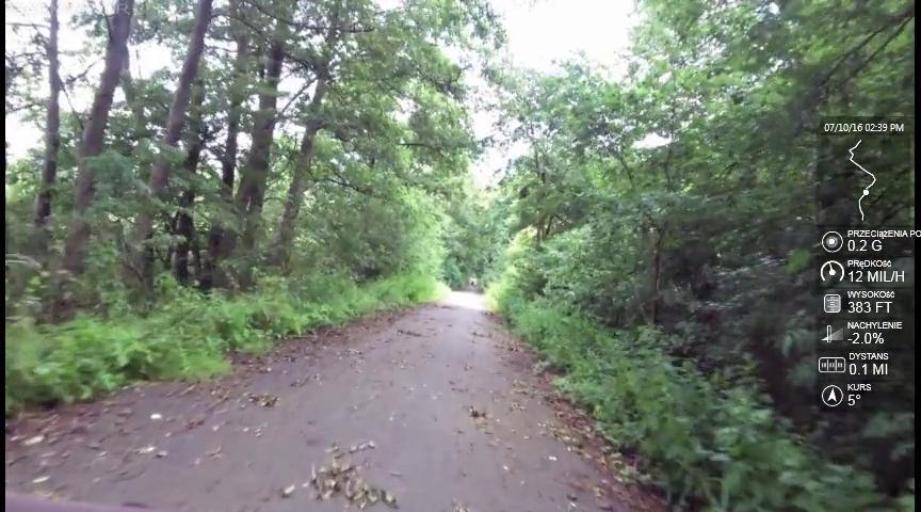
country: PL
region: West Pomeranian Voivodeship
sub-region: Powiat gryfinski
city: Banie
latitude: 53.0786
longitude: 14.6367
